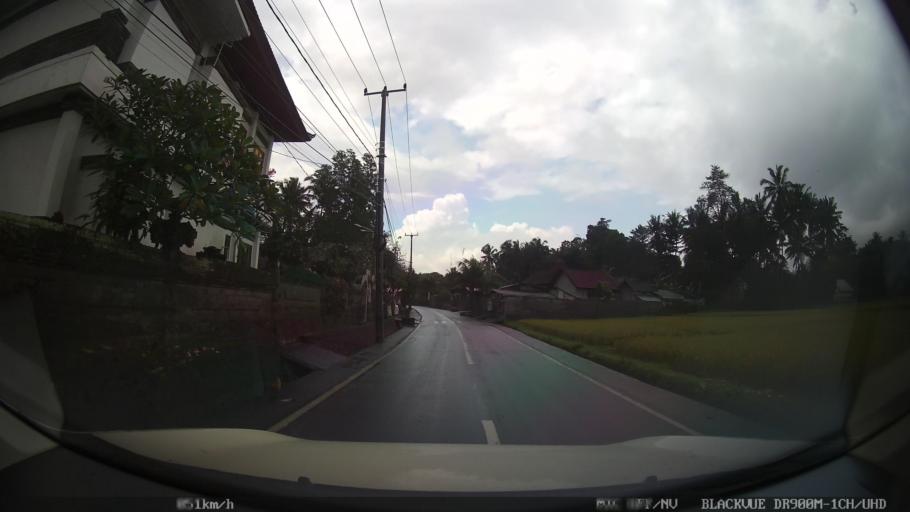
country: ID
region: Bali
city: Banjar Teguan
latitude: -8.5112
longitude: 115.2292
